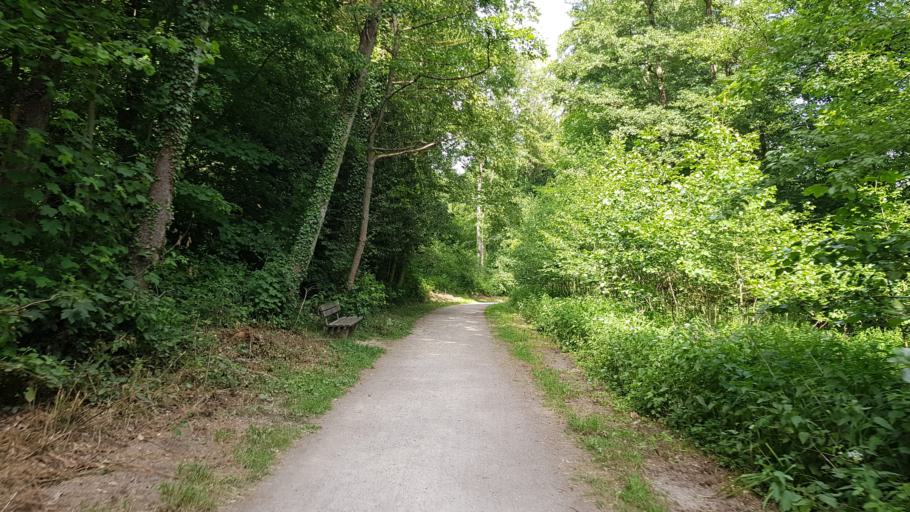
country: DE
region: North Rhine-Westphalia
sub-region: Regierungsbezirk Dusseldorf
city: Muelheim (Ruhr)
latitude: 51.4075
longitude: 6.9133
